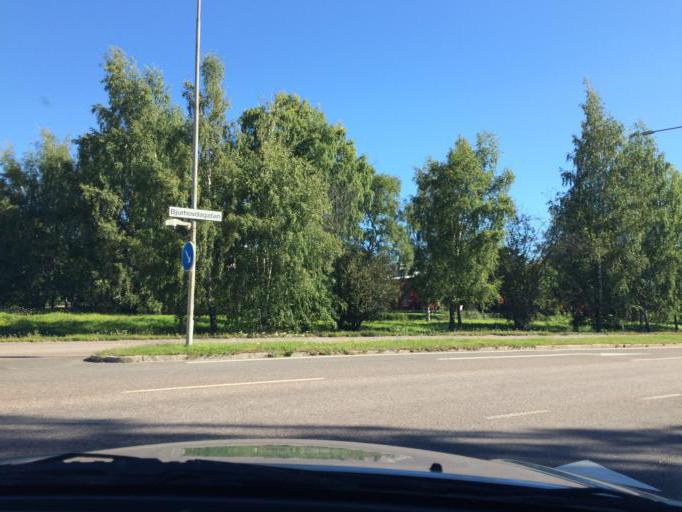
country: SE
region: Vaestmanland
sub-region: Vasteras
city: Hokasen
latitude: 59.6237
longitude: 16.6129
